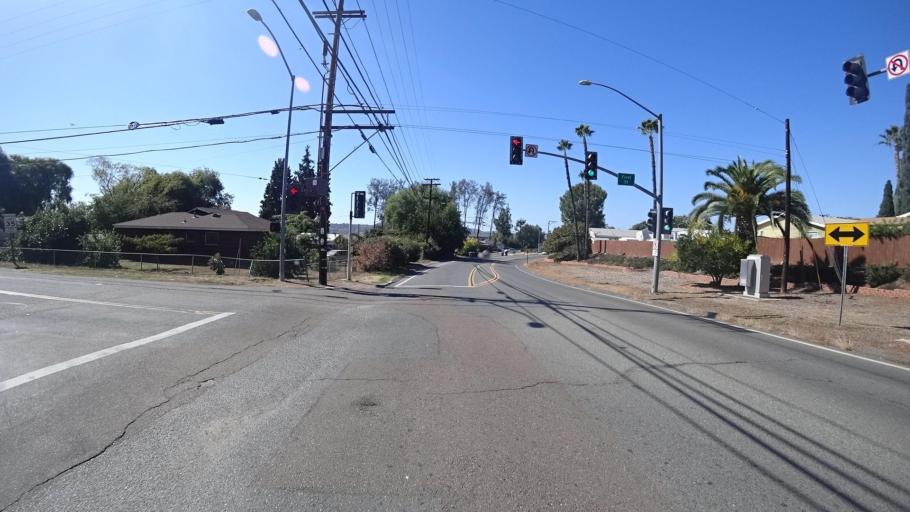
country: US
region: California
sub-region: San Diego County
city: Winter Gardens
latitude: 32.8213
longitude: -116.9446
